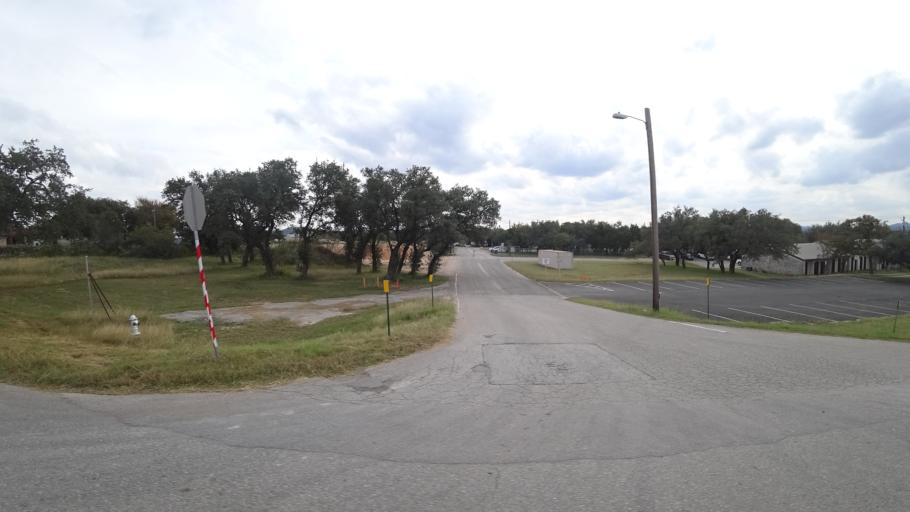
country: US
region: Texas
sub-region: Travis County
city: Hudson Bend
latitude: 30.3876
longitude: -97.8986
